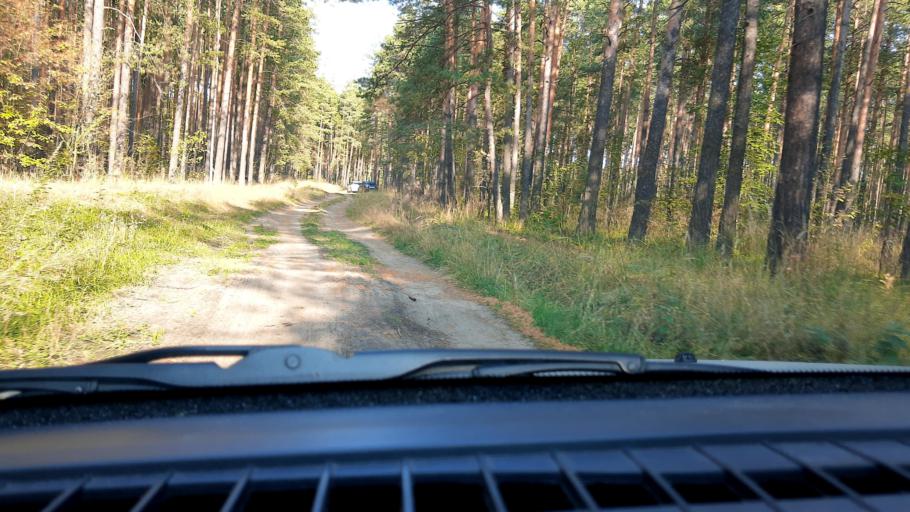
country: RU
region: Nizjnij Novgorod
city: Lukino
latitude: 56.3971
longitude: 43.6438
